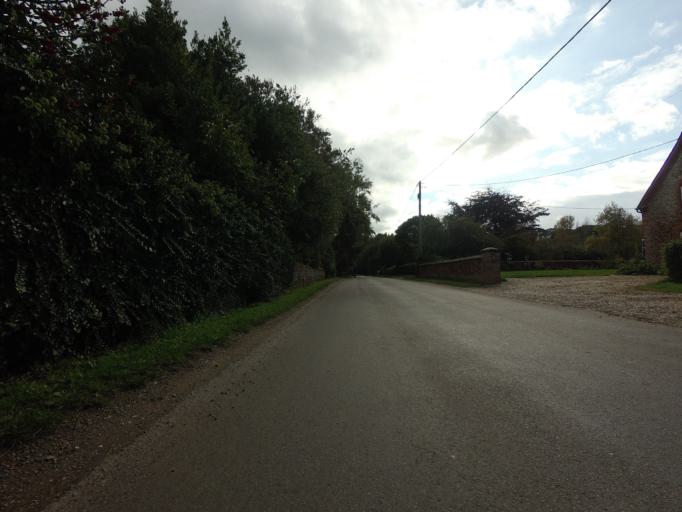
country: GB
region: England
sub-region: Norfolk
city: Snettisham
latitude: 52.8662
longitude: 0.5081
